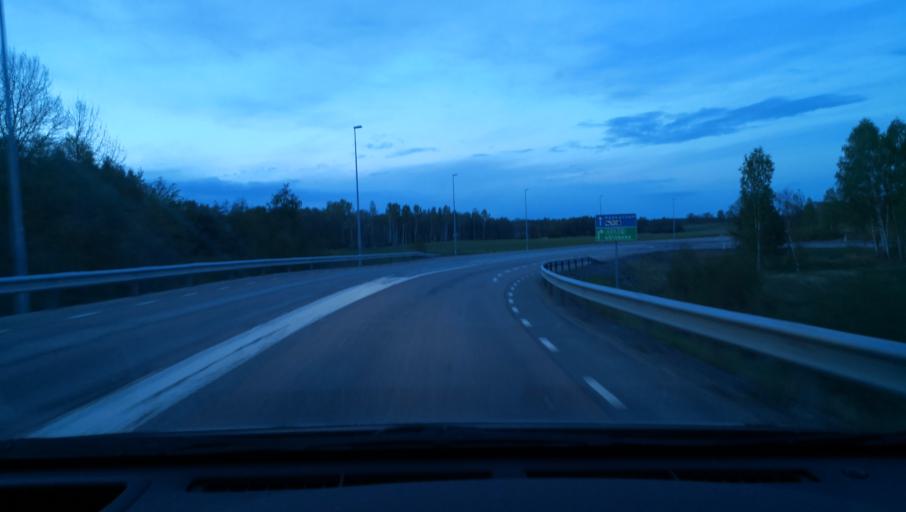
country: SE
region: OErebro
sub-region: Lekebergs Kommun
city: Fjugesta
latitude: 59.0352
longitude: 14.8707
